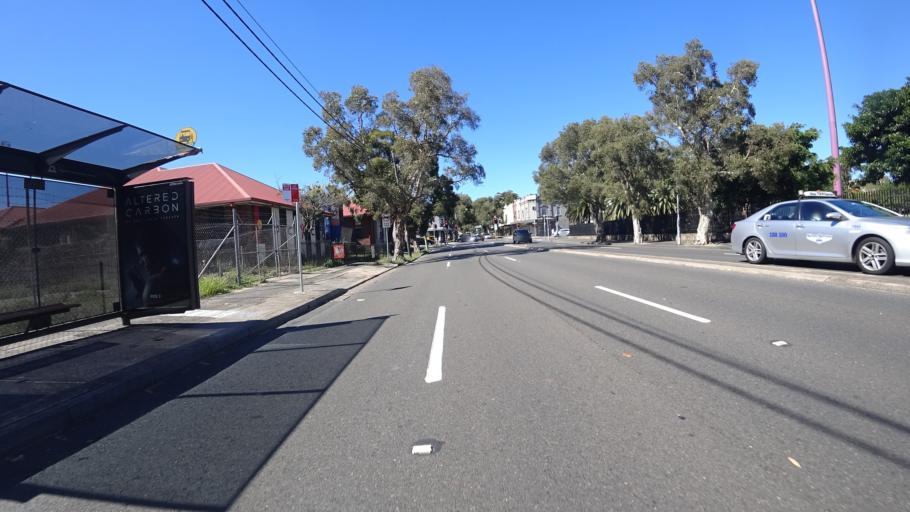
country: AU
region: New South Wales
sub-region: City of Sydney
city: Redfern
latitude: -33.8954
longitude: 151.2070
